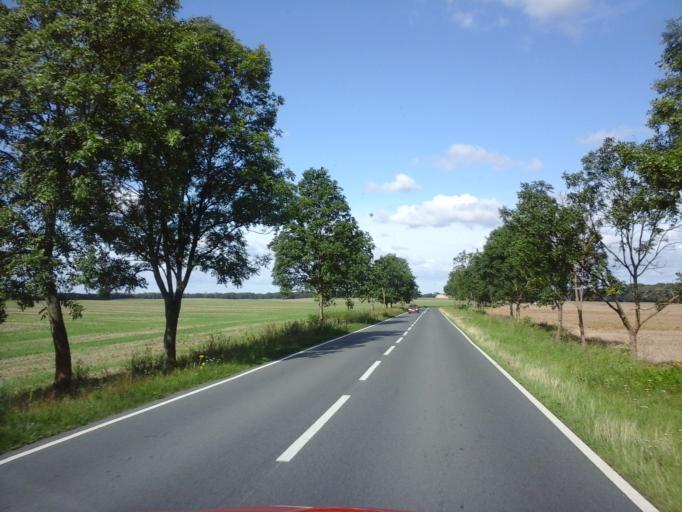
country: PL
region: West Pomeranian Voivodeship
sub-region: Powiat stargardzki
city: Dolice
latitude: 53.1978
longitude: 15.1771
